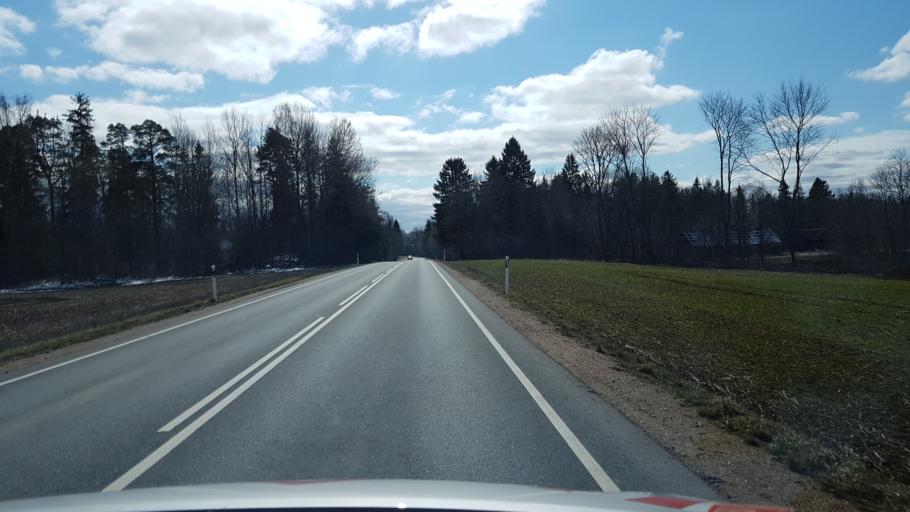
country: EE
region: Laeaene-Virumaa
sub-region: Tapa vald
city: Tapa
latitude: 59.3604
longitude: 26.0003
